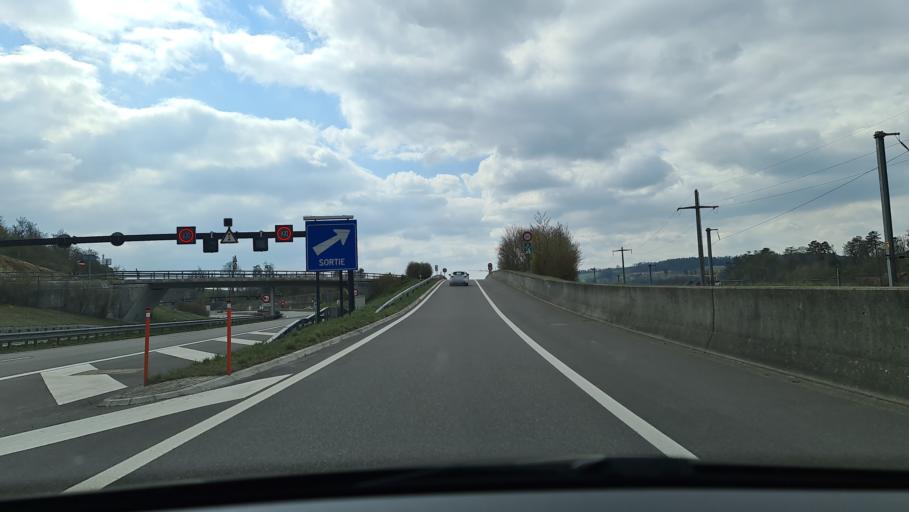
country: CH
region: Jura
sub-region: Porrentruy District
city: Fontenais
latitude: 47.4169
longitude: 7.0984
